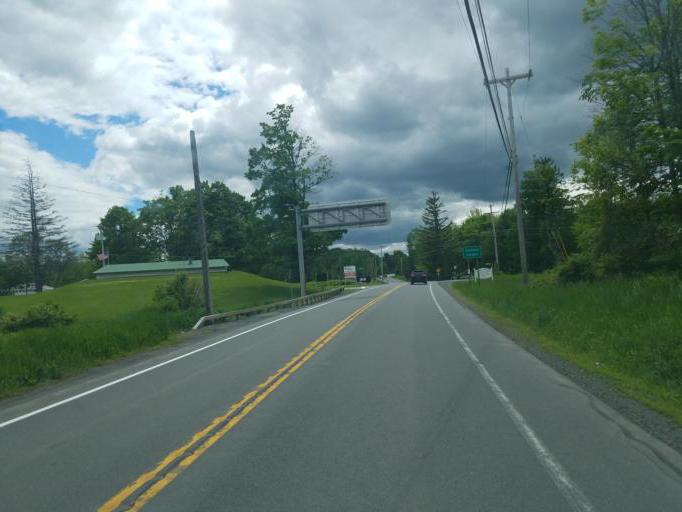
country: US
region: New York
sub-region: Herkimer County
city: Mohawk
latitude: 42.9615
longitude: -75.0138
